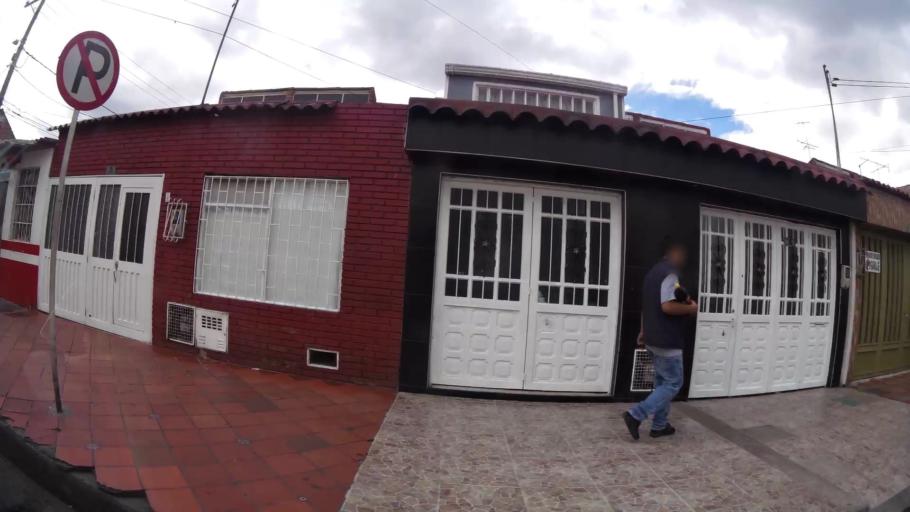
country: CO
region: Bogota D.C.
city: Bogota
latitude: 4.6131
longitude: -74.1269
